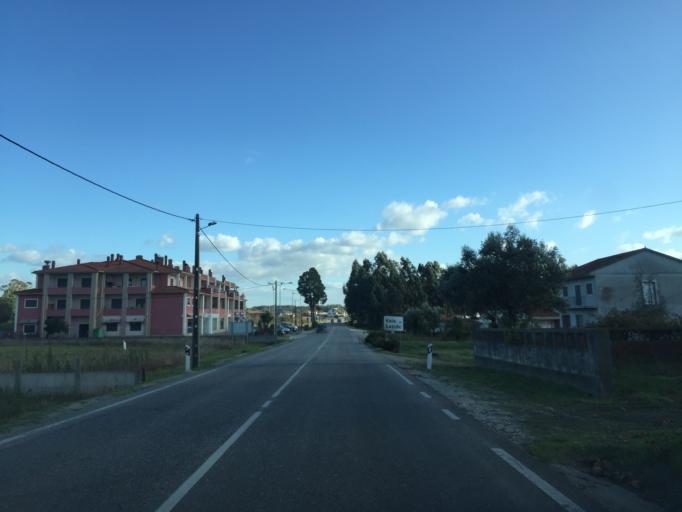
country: PT
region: Leiria
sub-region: Pombal
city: Lourical
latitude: 39.9617
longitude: -8.7890
